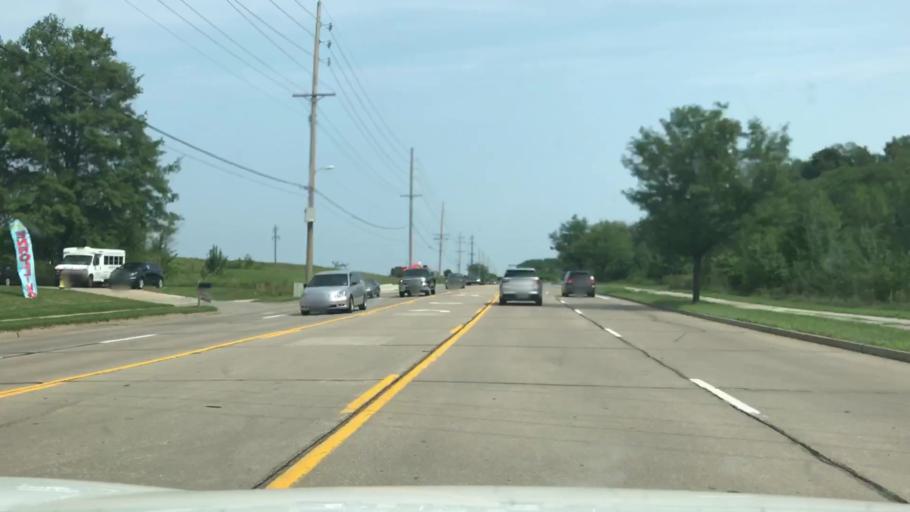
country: US
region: Missouri
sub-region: Saint Charles County
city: Dardenne Prairie
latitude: 38.7961
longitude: -90.7360
